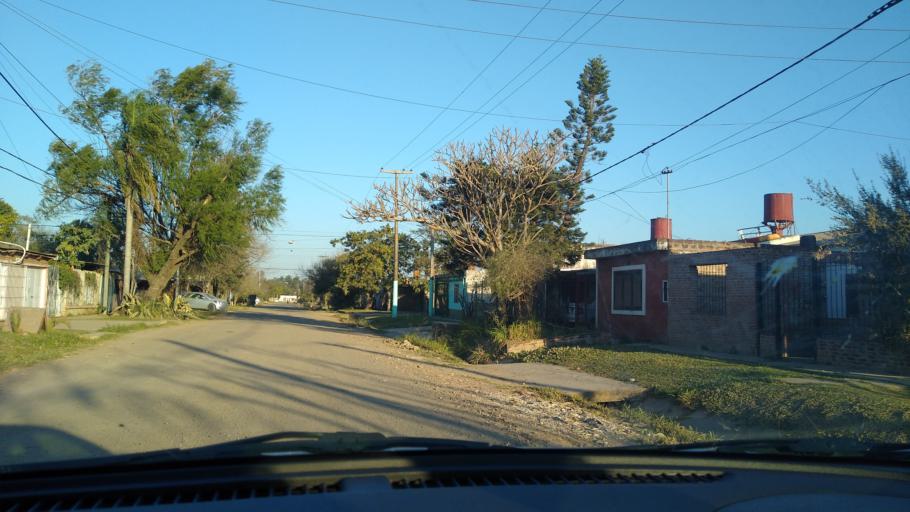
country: AR
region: Chaco
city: Resistencia
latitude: -27.4882
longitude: -58.9759
